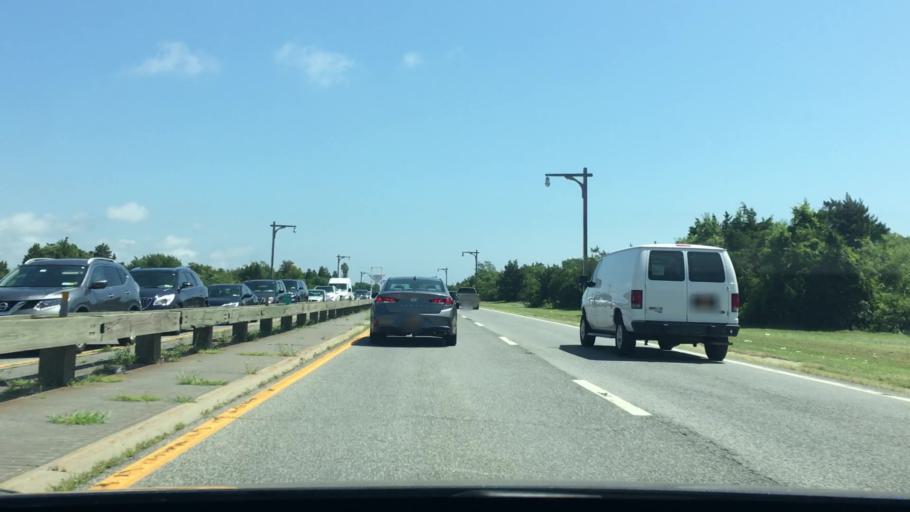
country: US
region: New York
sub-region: Nassau County
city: Point Lookout
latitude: 40.6062
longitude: -73.5622
